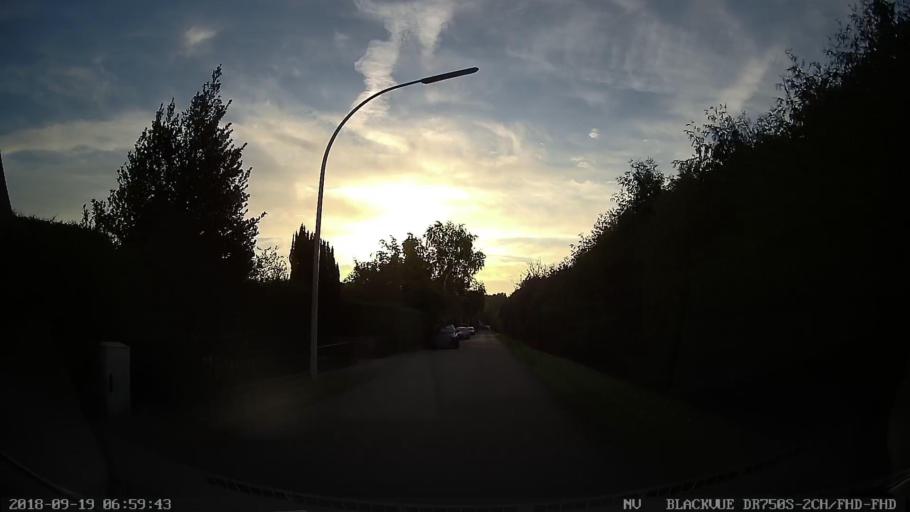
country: DE
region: Hamburg
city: Eidelstedt
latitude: 53.6328
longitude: 9.8919
